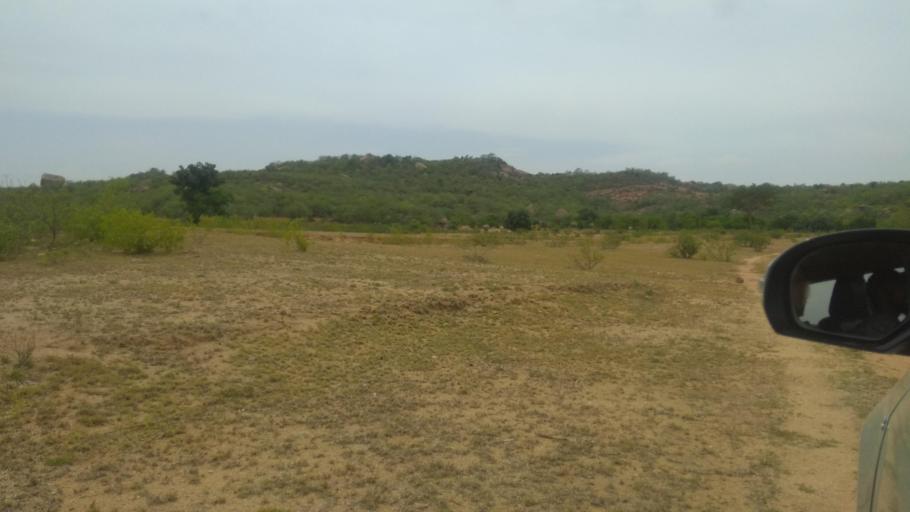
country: IN
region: Telangana
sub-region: Mahbubnagar
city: Farrukhnagar
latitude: 16.8904
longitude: 78.4872
